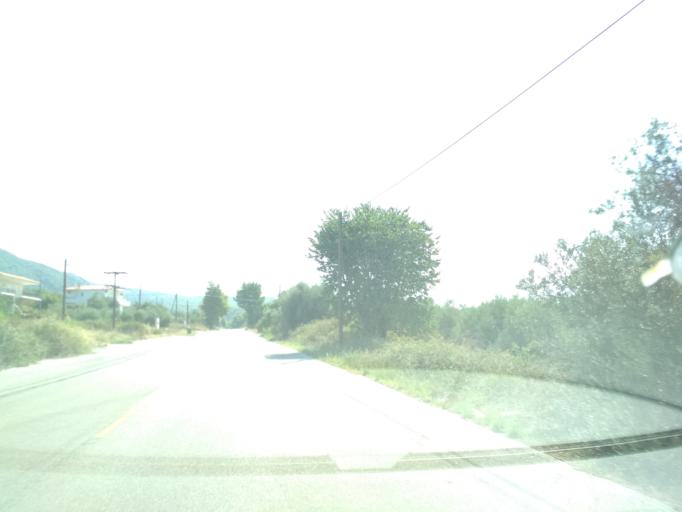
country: GR
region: Central Greece
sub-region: Nomos Evvoias
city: Roviai
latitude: 38.8306
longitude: 23.2080
